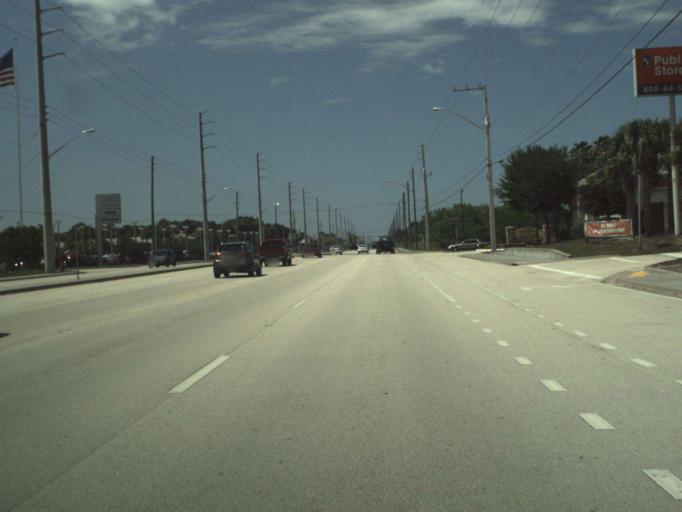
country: US
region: Florida
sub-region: Saint Lucie County
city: Indian River Estates
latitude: 27.3569
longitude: -80.3258
